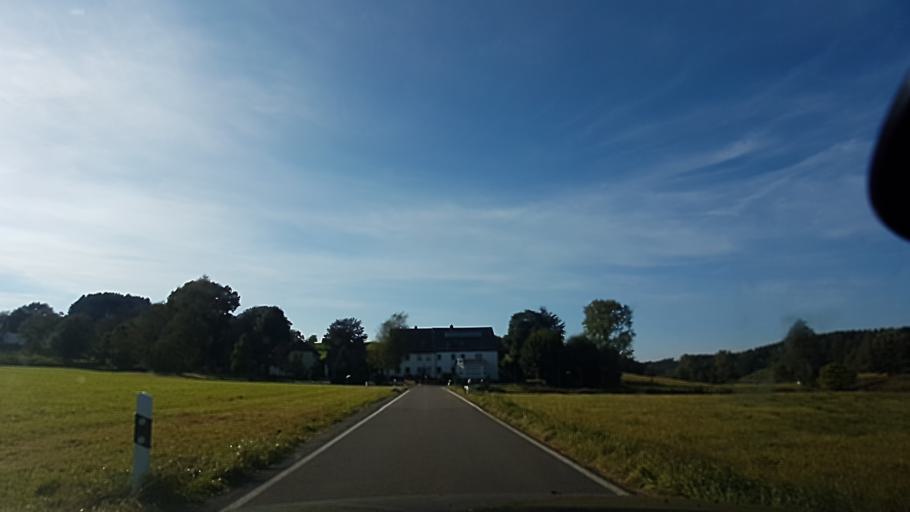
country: DE
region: North Rhine-Westphalia
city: Kierspe
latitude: 51.1353
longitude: 7.5763
